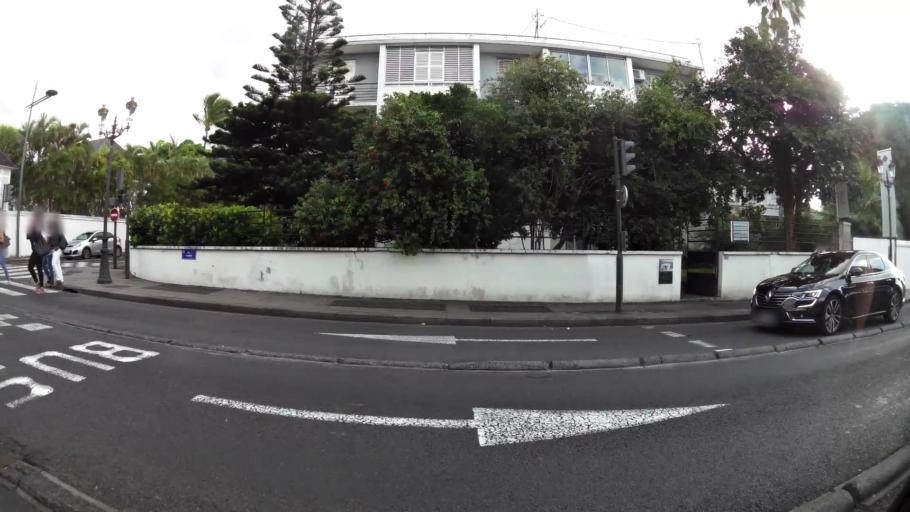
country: RE
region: Reunion
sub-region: Reunion
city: Saint-Denis
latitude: -20.8811
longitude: 55.4494
